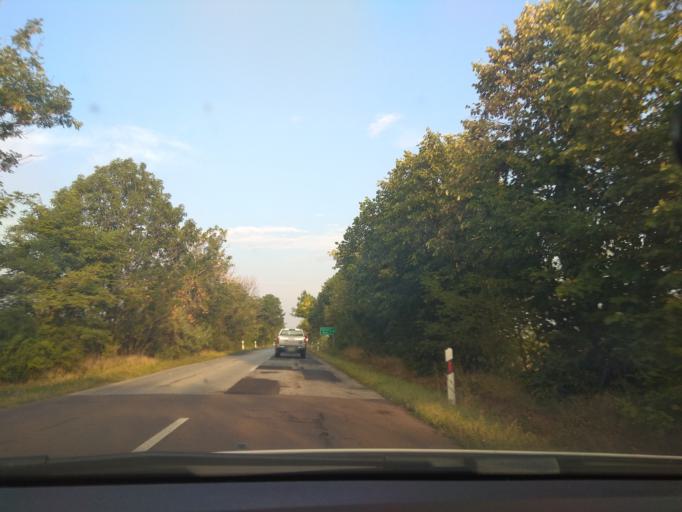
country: HU
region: Heves
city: Szihalom
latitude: 47.8208
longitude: 20.4955
